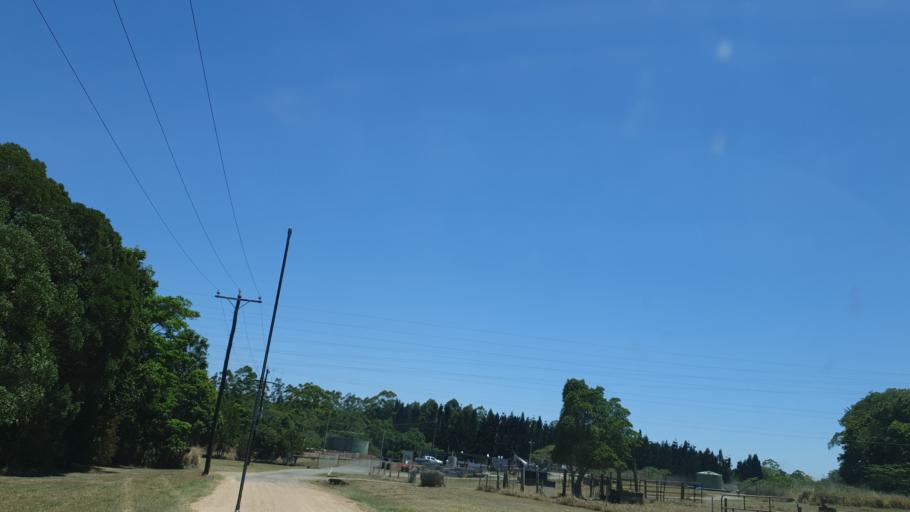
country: AU
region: Queensland
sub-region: Tablelands
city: Atherton
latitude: -17.2557
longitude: 145.4799
